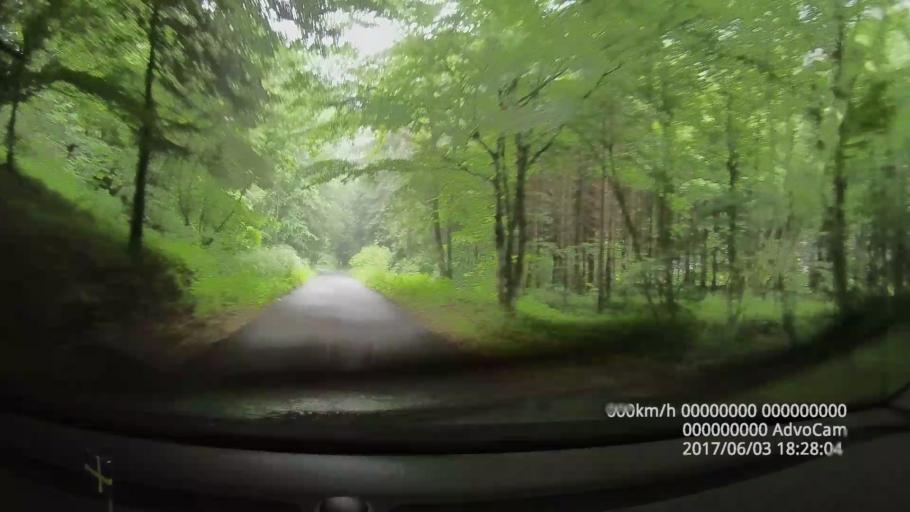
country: RO
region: Gorj
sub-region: Comuna Runcu
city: Dobrita
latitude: 45.1589
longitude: 23.1959
